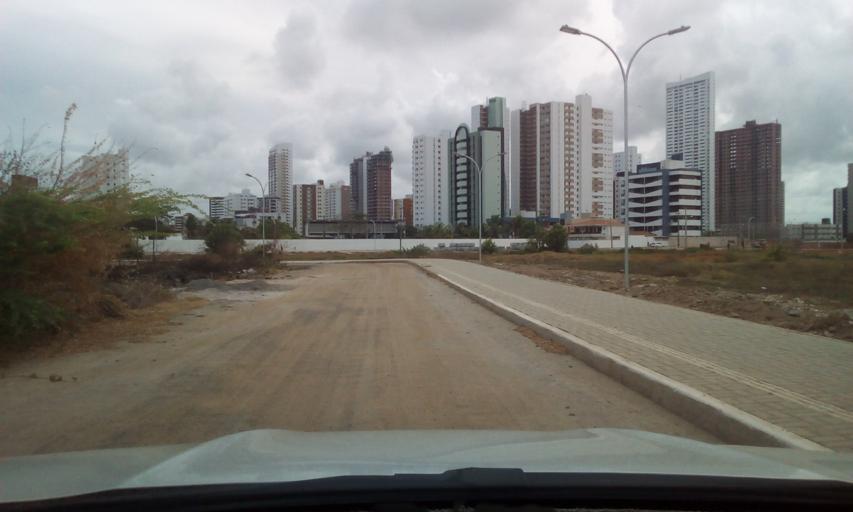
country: BR
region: Paraiba
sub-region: Joao Pessoa
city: Joao Pessoa
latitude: -7.0783
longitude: -34.8353
